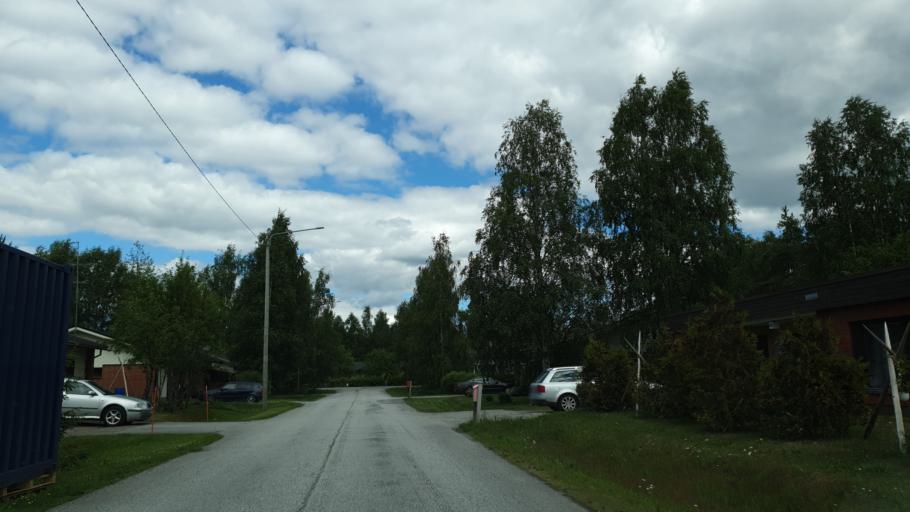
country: FI
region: Kainuu
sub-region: Kehys-Kainuu
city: Kuhmo
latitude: 64.1155
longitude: 29.4804
